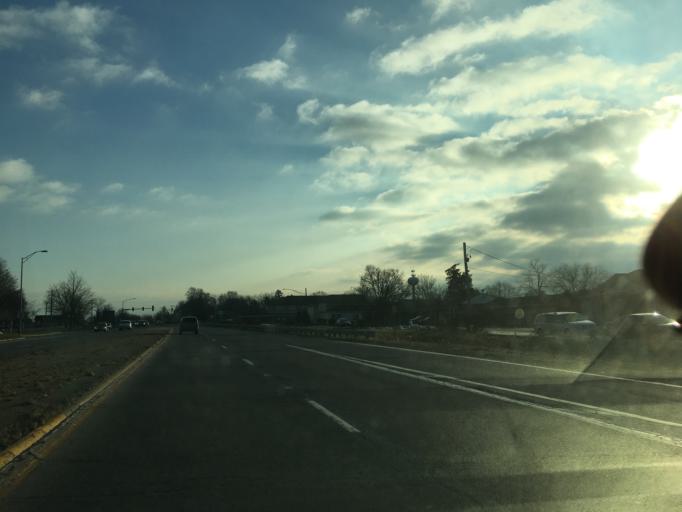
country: US
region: Illinois
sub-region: Kane County
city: Sugar Grove
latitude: 41.7642
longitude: -88.4427
